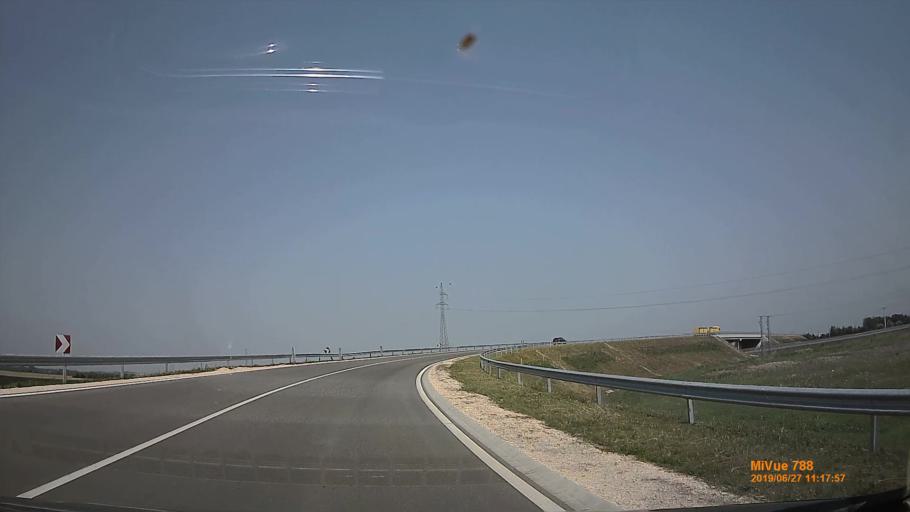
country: HU
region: Pest
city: Cegled
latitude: 47.2000
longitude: 19.7844
